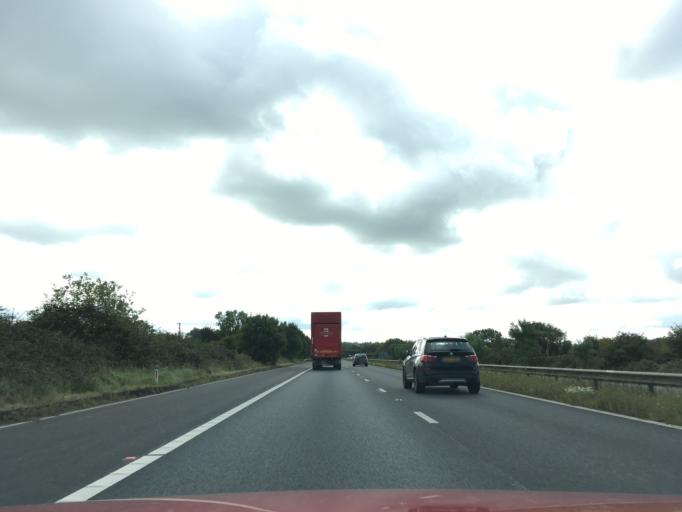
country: GB
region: England
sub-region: South Gloucestershire
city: Almondsbury
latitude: 51.5802
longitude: -2.5909
